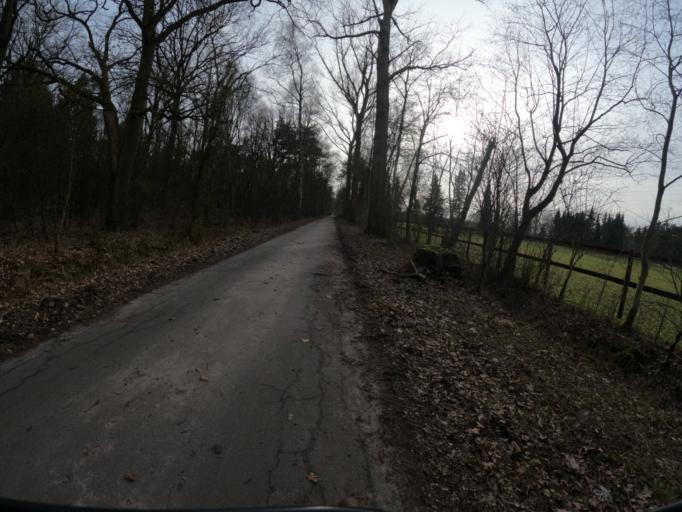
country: DE
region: Schleswig-Holstein
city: Appen
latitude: 53.6119
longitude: 9.7369
